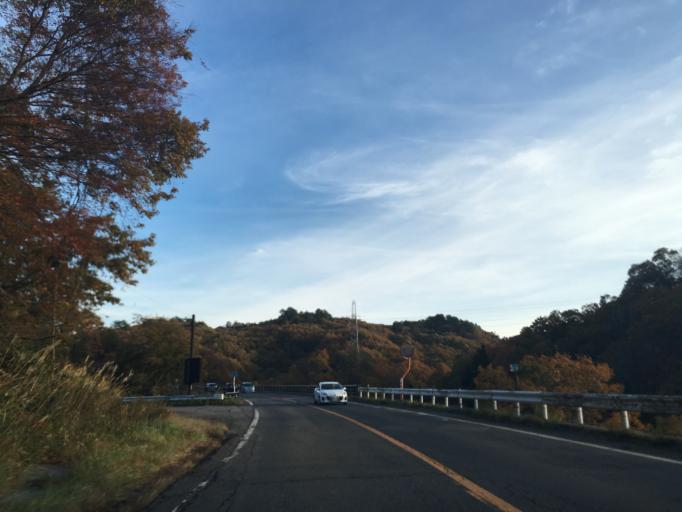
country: JP
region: Fukushima
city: Kitakata
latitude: 37.5711
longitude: 139.7105
